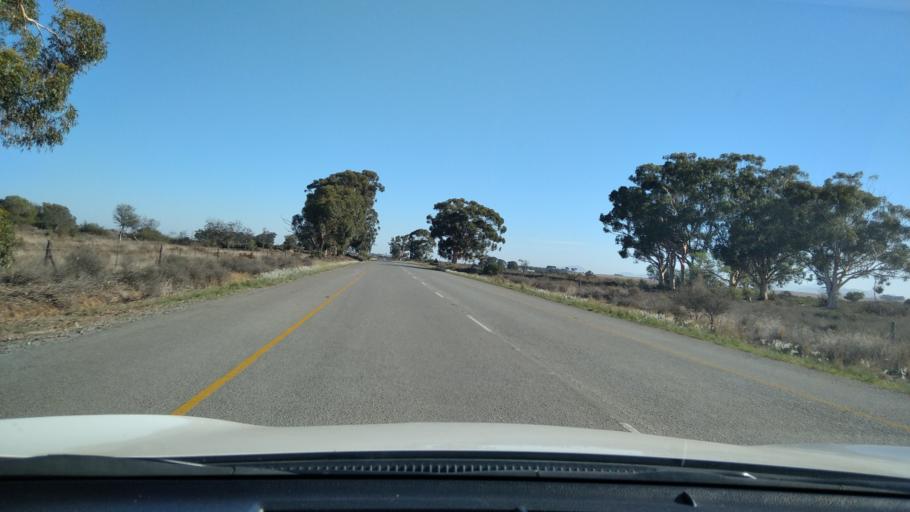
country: ZA
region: Western Cape
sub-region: West Coast District Municipality
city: Moorreesburg
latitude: -33.2725
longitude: 18.6002
